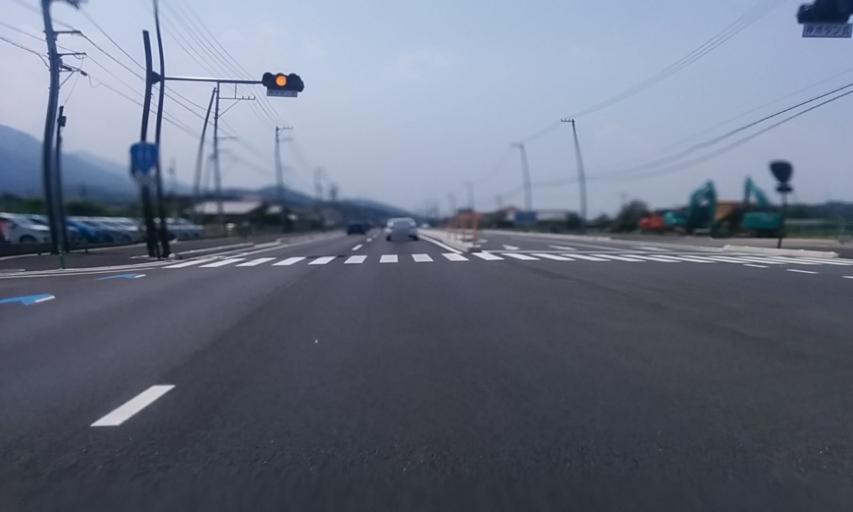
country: JP
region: Ehime
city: Niihama
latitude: 33.9244
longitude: 133.2567
